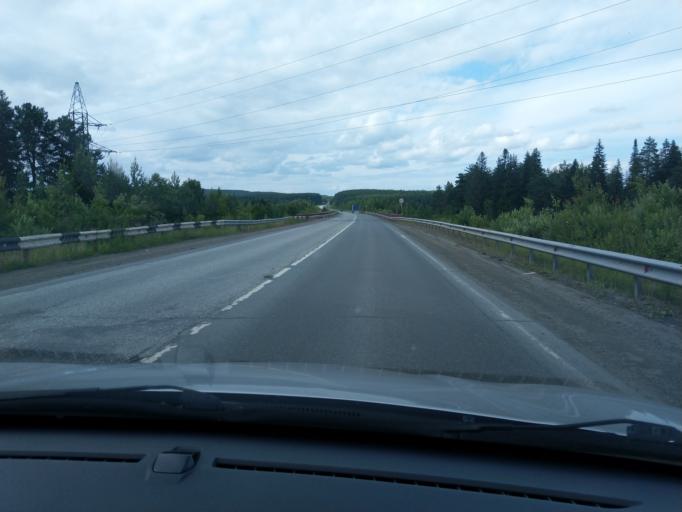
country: RU
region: Sverdlovsk
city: Nizhniy Tagil
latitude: 57.9347
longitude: 59.8663
